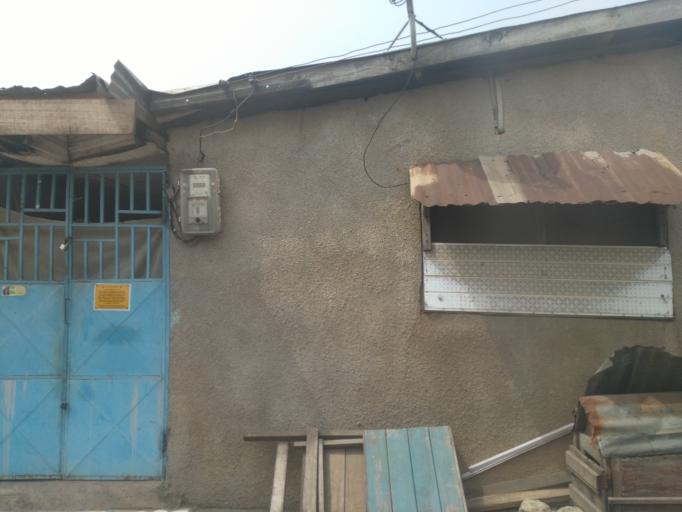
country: GH
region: Ashanti
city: Kumasi
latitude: 6.7014
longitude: -1.6096
